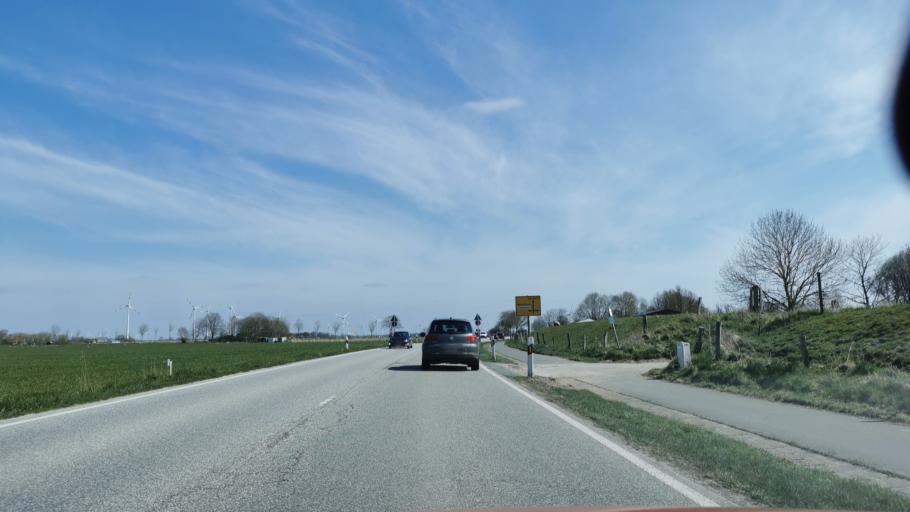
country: DE
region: Schleswig-Holstein
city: Oesterdeichstrich
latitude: 54.1592
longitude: 8.8967
